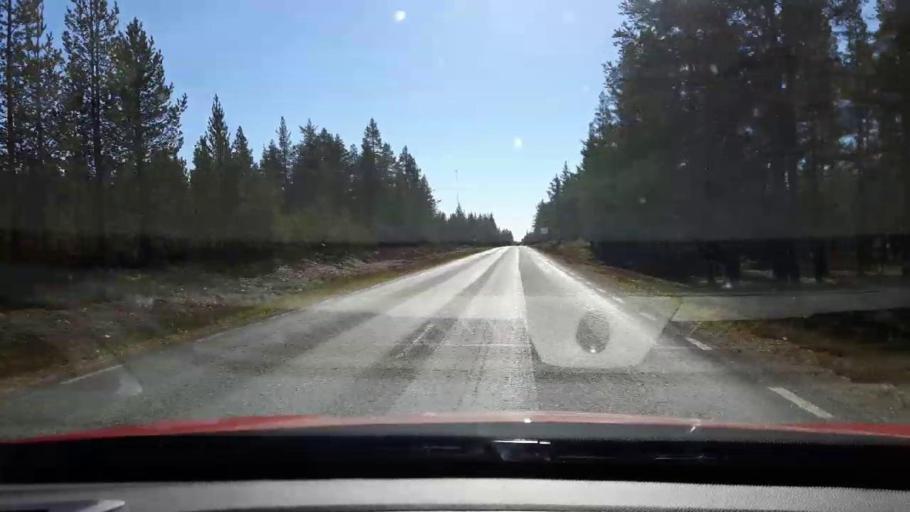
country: SE
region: Jaemtland
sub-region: Harjedalens Kommun
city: Sveg
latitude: 62.4131
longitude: 13.9174
